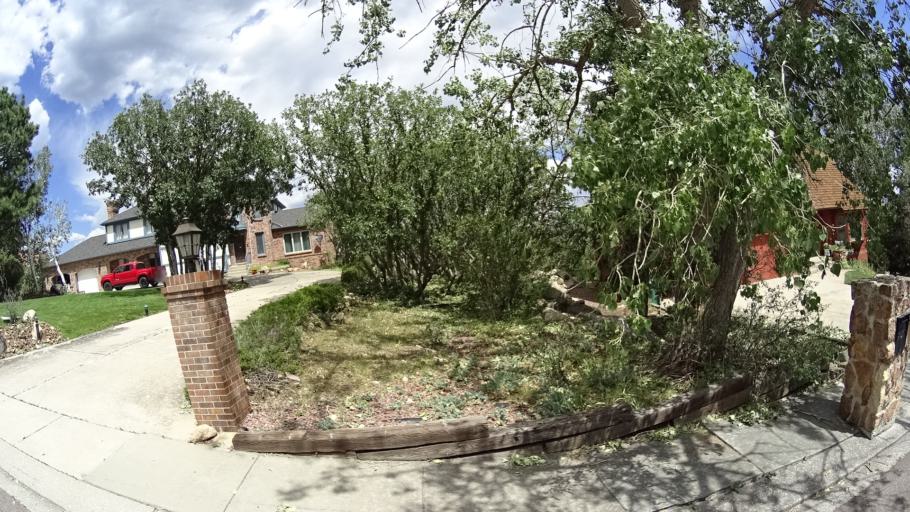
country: US
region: Colorado
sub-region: El Paso County
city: Stratmoor
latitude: 38.7694
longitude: -104.8238
